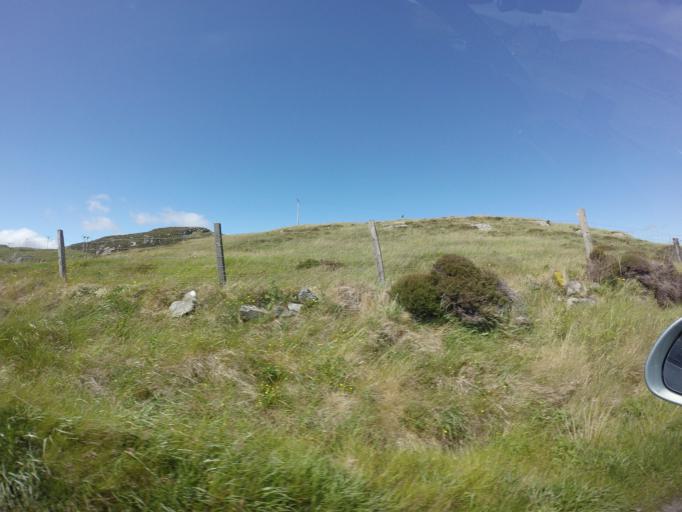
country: GB
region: Scotland
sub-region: Eilean Siar
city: Stornoway
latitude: 58.0965
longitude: -6.5810
